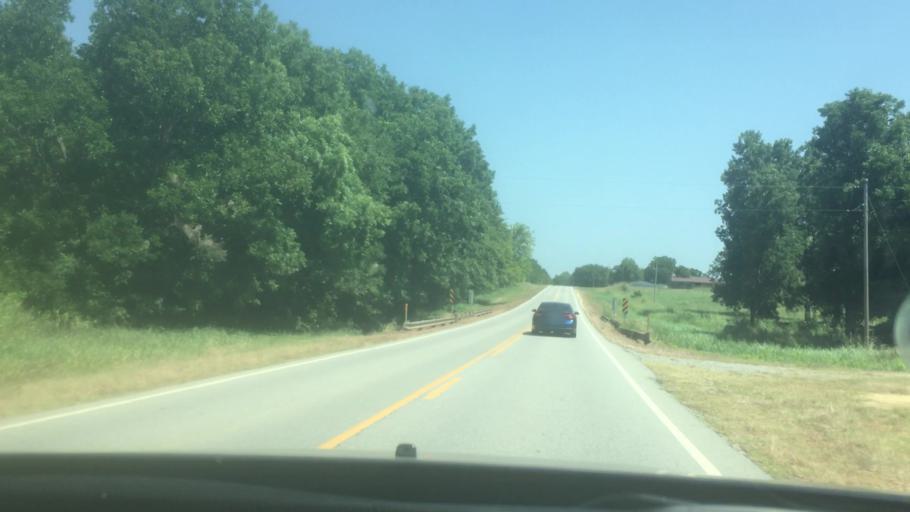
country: US
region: Oklahoma
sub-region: Coal County
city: Coalgate
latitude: 34.5269
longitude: -96.4070
